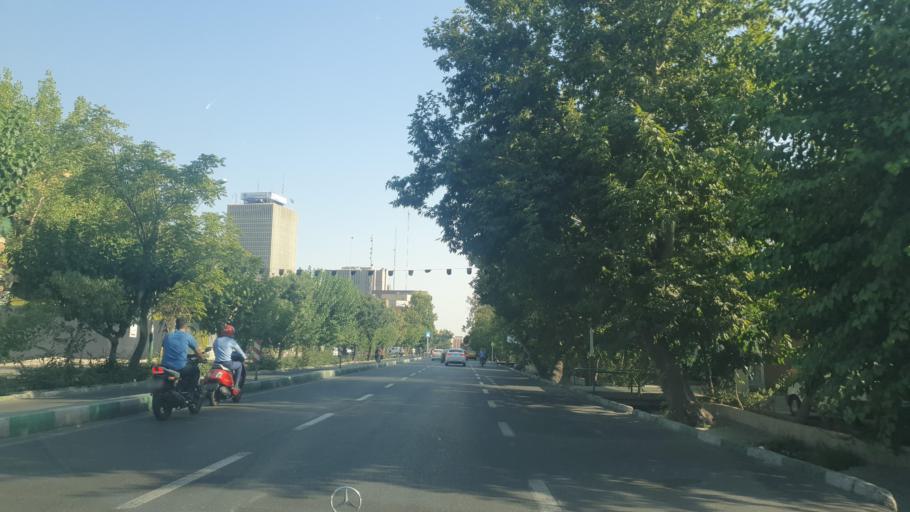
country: IR
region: Tehran
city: Tehran
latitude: 35.7107
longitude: 51.4255
